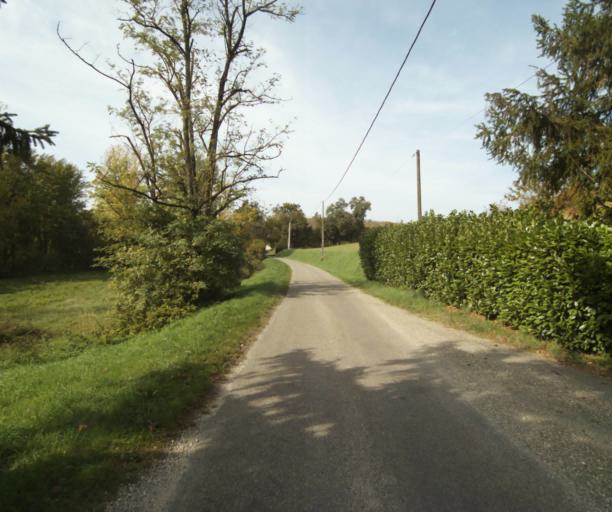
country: FR
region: Midi-Pyrenees
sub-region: Departement du Tarn-et-Garonne
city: Corbarieu
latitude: 43.9599
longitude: 1.3706
